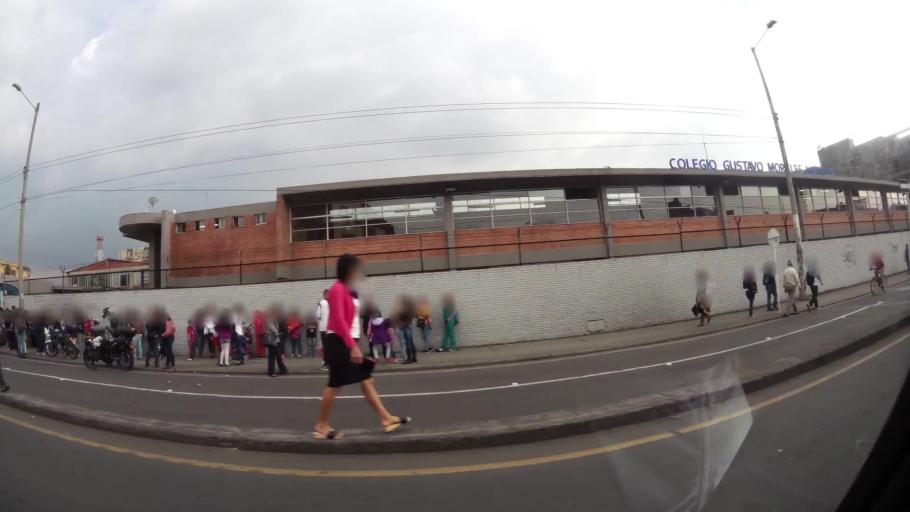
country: CO
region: Bogota D.C.
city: Barrio San Luis
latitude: 4.7169
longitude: -74.0645
